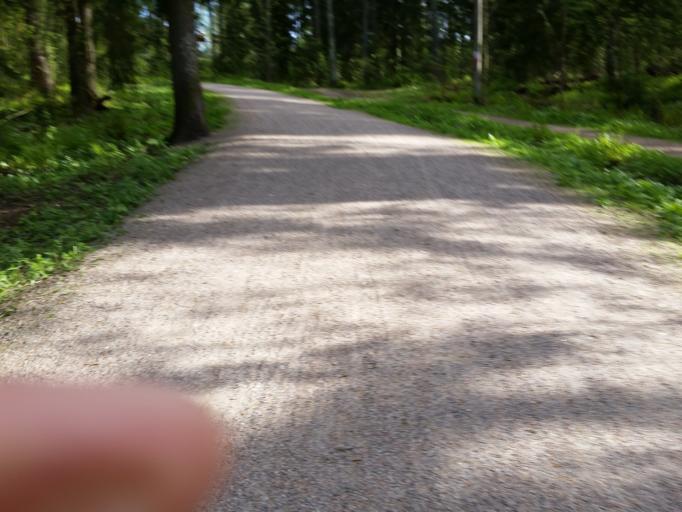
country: FI
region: Uusimaa
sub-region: Helsinki
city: Kauniainen
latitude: 60.1775
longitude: 24.7282
